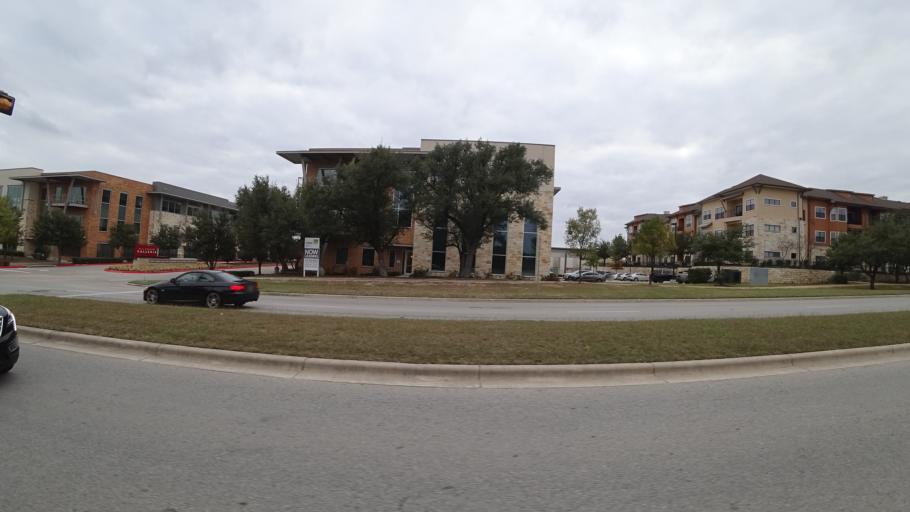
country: US
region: Texas
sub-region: Travis County
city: Bee Cave
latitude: 30.3109
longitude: -97.9391
